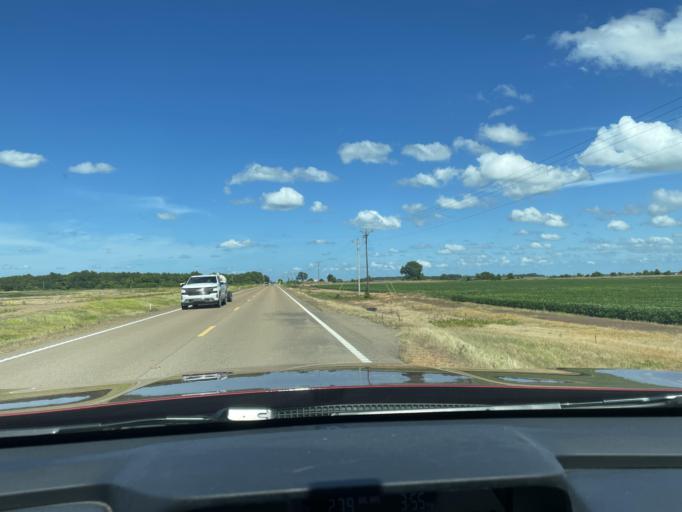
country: US
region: Mississippi
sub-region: Humphreys County
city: Belzoni
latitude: 33.1826
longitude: -90.6384
